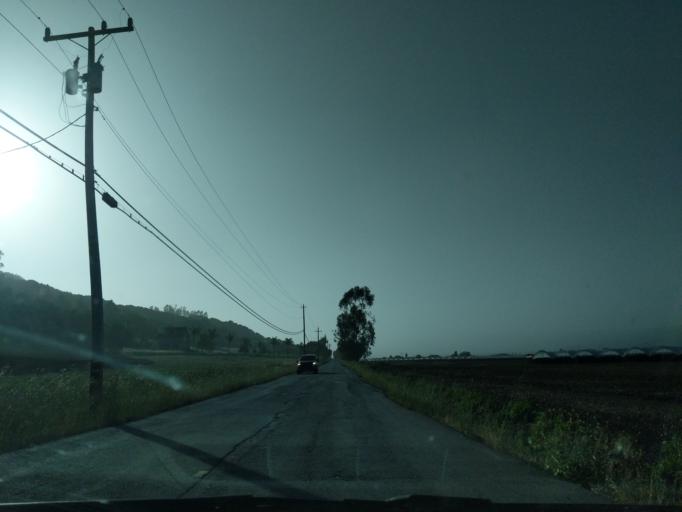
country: US
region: California
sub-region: San Benito County
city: Aromas
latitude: 36.8863
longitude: -121.6843
